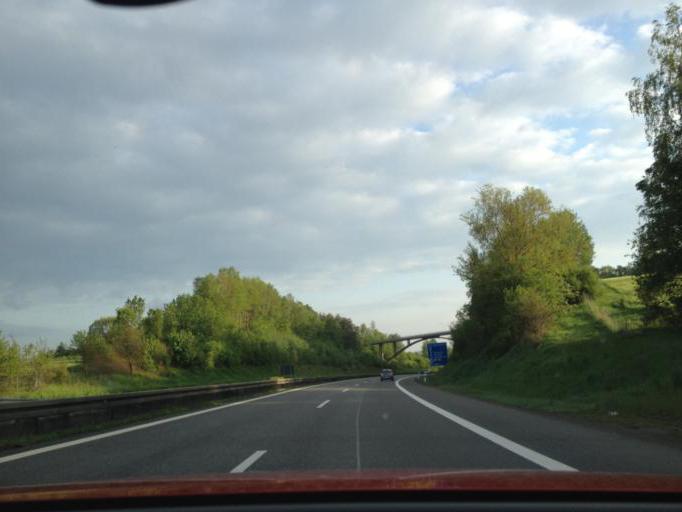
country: DE
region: Bavaria
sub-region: Upper Palatinate
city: Neustadt an der Waldnaab
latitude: 49.7302
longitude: 12.1569
